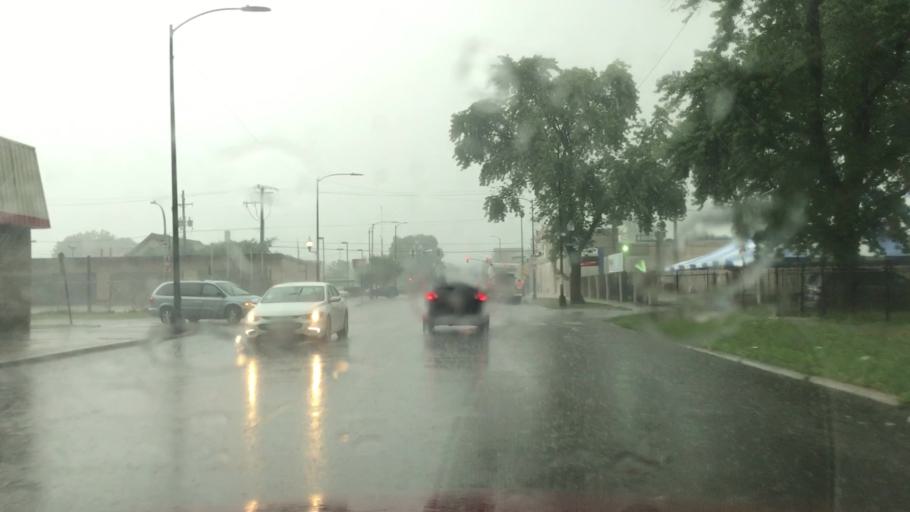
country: US
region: Illinois
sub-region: Cook County
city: Oak Park
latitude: 41.8789
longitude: -87.7550
